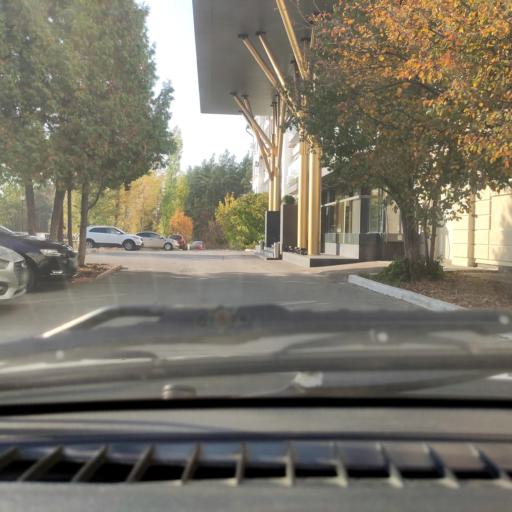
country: RU
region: Samara
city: Tol'yatti
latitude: 53.4744
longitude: 49.3548
